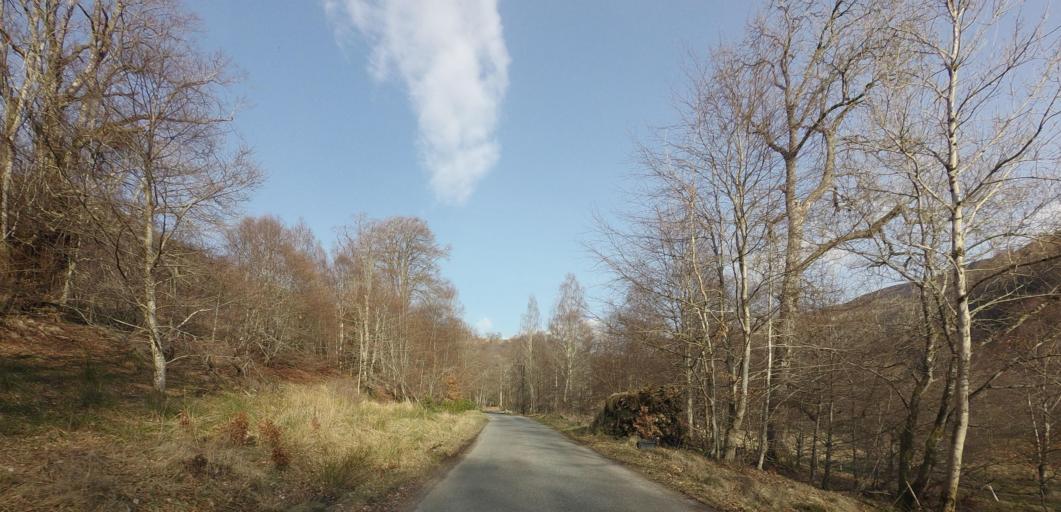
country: GB
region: Scotland
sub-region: Perth and Kinross
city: Comrie
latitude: 56.5983
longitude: -4.1144
